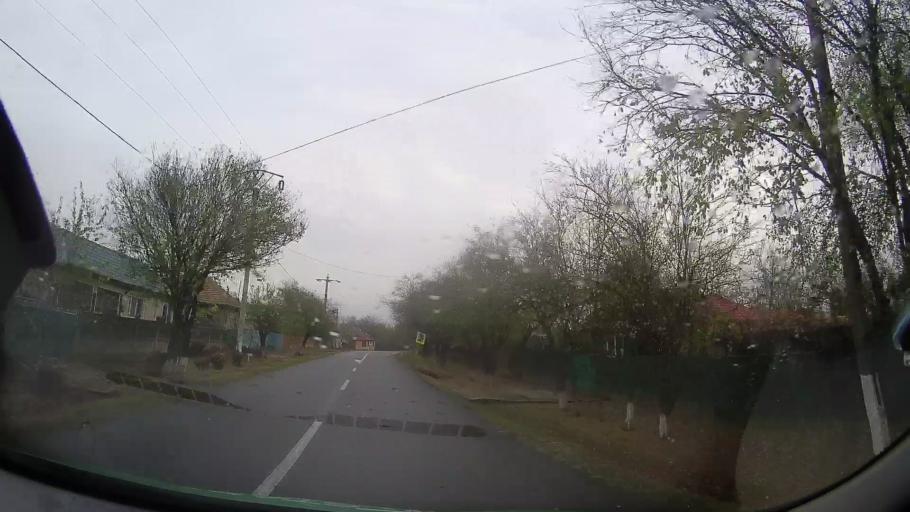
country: RO
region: Ialomita
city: Brazii
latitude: 44.7800
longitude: 26.3309
